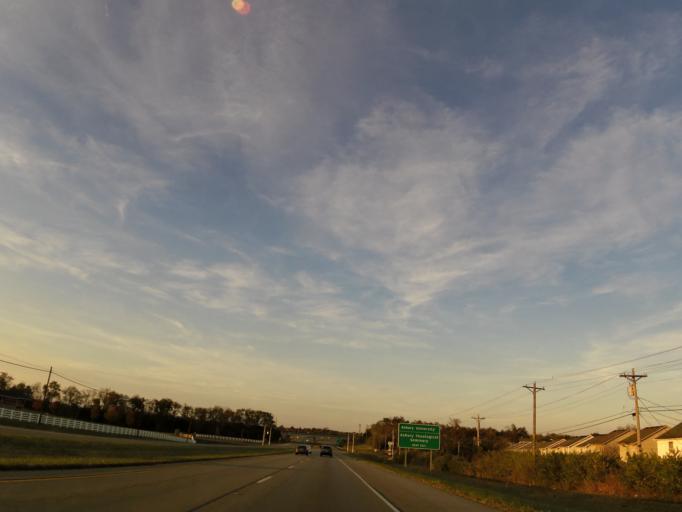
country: US
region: Kentucky
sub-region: Jessamine County
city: Nicholasville
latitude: 37.8748
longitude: -84.5973
